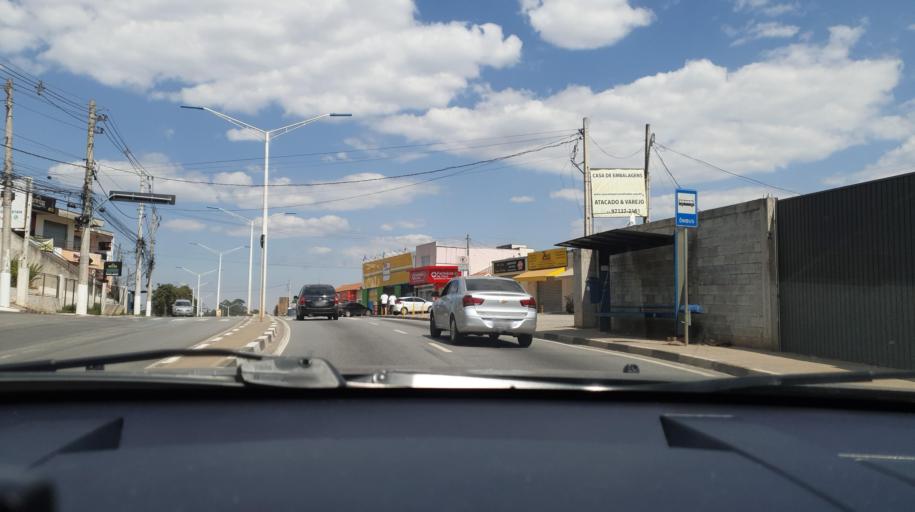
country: BR
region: Sao Paulo
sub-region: Vargem Grande Paulista
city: Vargem Grande Paulista
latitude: -23.6463
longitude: -46.9936
